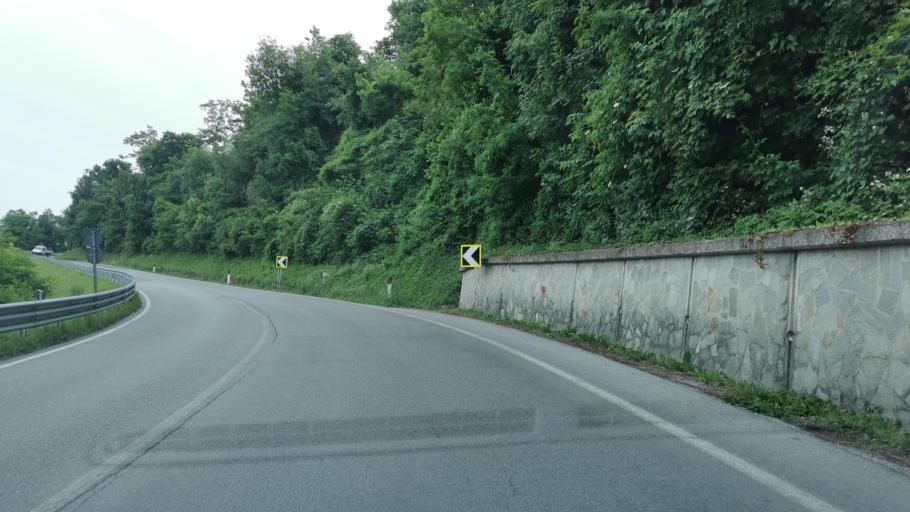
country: IT
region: Piedmont
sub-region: Provincia di Cuneo
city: Ceva
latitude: 44.3805
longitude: 8.0390
